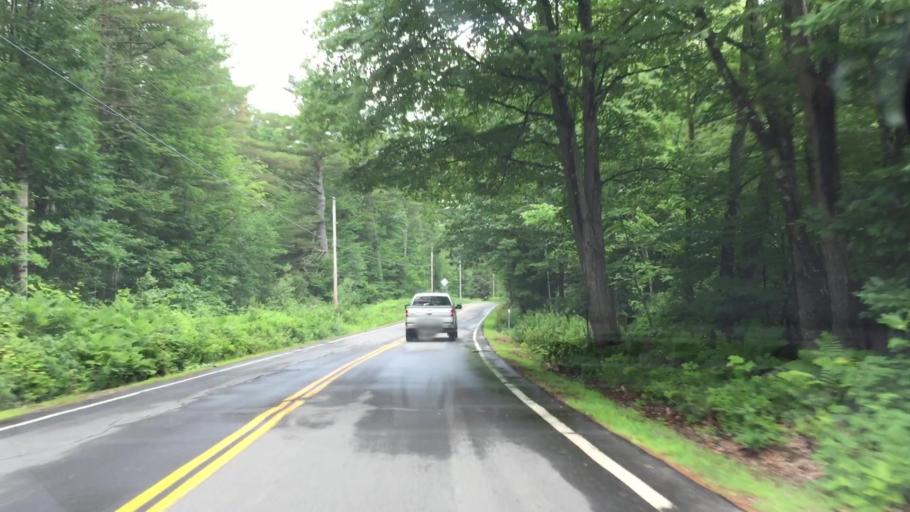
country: US
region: New Hampshire
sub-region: Carroll County
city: Sandwich
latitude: 43.8028
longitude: -71.4730
